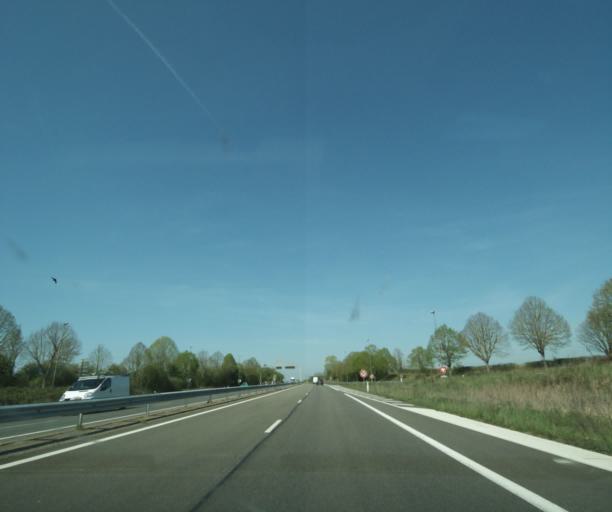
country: FR
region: Bourgogne
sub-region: Departement de la Nievre
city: La Charite-sur-Loire
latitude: 47.1857
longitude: 3.0365
